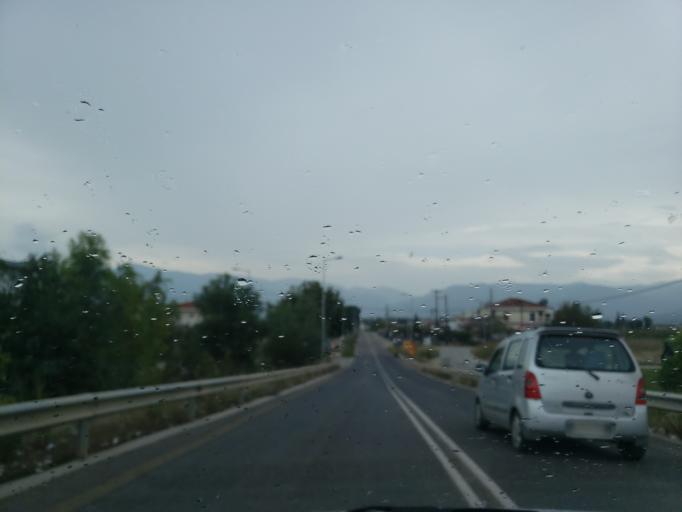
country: GR
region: Central Greece
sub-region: Nomos Fthiotidos
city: Rodhitsa
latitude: 38.8659
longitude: 22.4397
